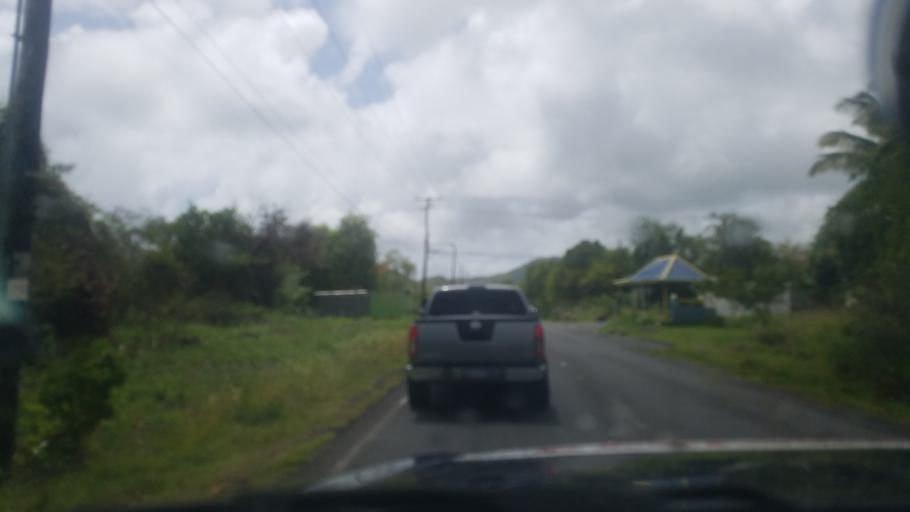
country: LC
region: Laborie Quarter
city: Laborie
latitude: 13.7405
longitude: -60.9760
